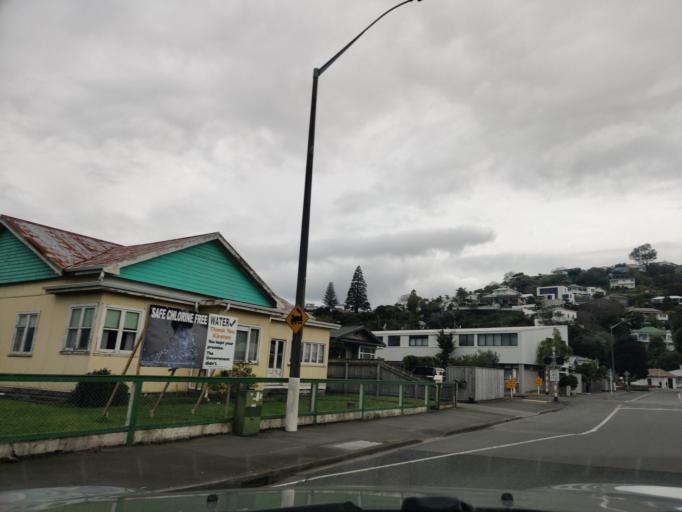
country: NZ
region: Hawke's Bay
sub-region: Napier City
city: Napier
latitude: -39.4789
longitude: 176.9076
